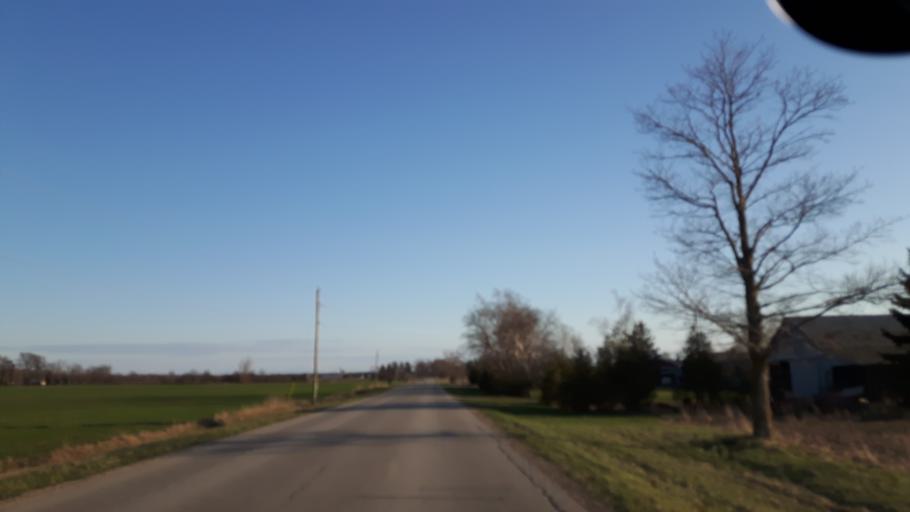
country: CA
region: Ontario
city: Goderich
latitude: 43.6483
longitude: -81.6846
